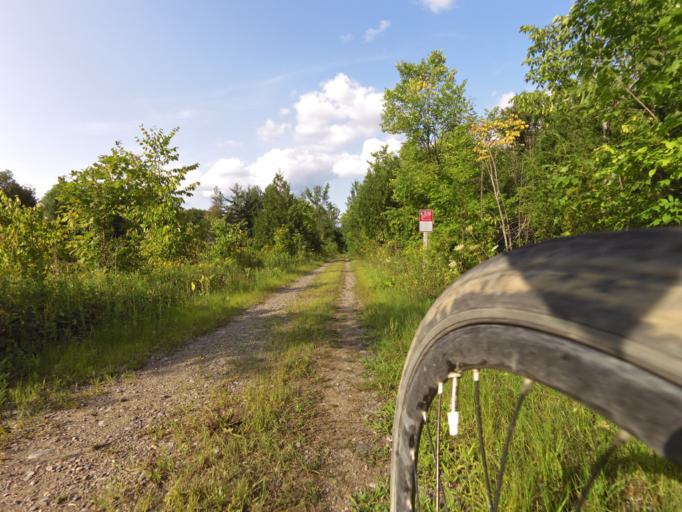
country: CA
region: Ontario
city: Kingston
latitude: 44.4526
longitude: -76.5225
